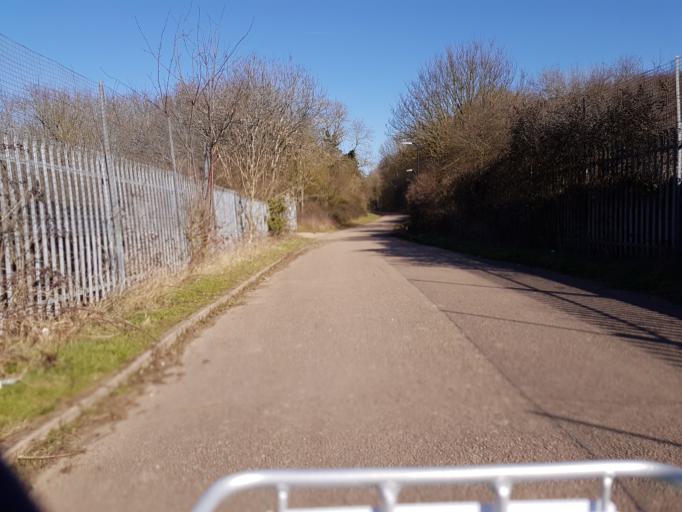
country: GB
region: England
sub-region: Milton Keynes
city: Milton Keynes
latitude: 52.0190
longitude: -0.7550
